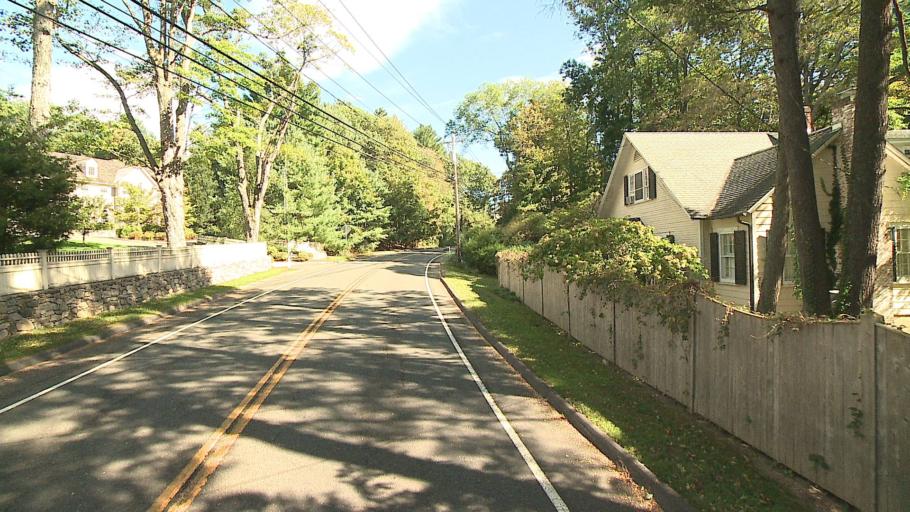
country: US
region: Connecticut
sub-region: Fairfield County
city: New Canaan
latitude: 41.1494
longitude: -73.4824
